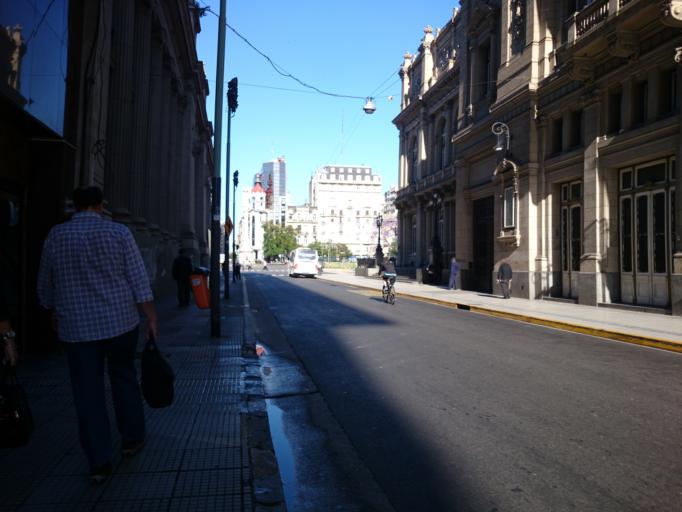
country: AR
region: Buenos Aires F.D.
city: Buenos Aires
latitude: -34.6015
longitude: -58.3830
